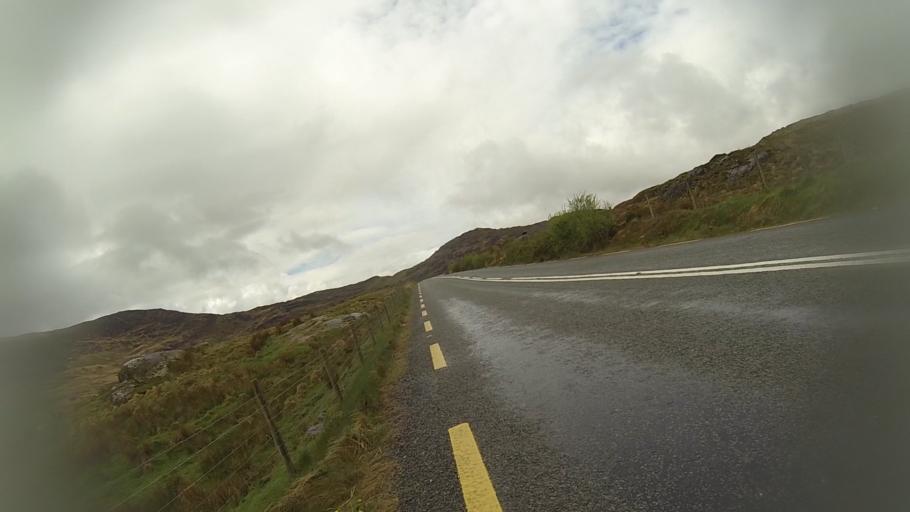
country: IE
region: Munster
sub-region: Ciarrai
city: Kenmare
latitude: 51.7983
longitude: -9.5790
